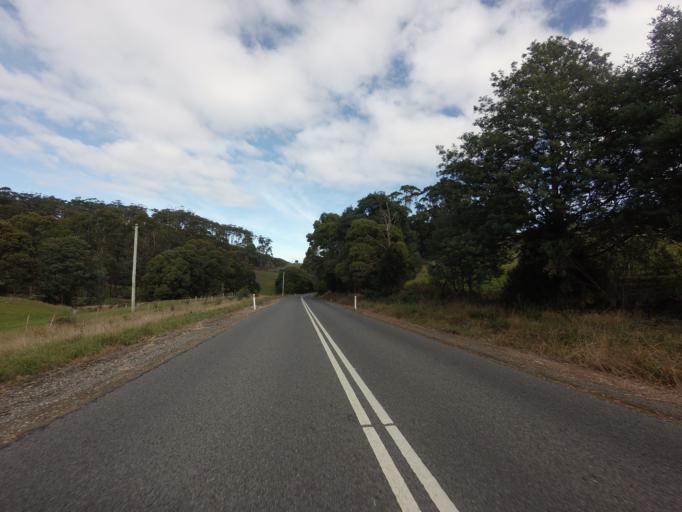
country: AU
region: Tasmania
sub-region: Clarence
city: Sandford
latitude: -43.0769
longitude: 147.7484
